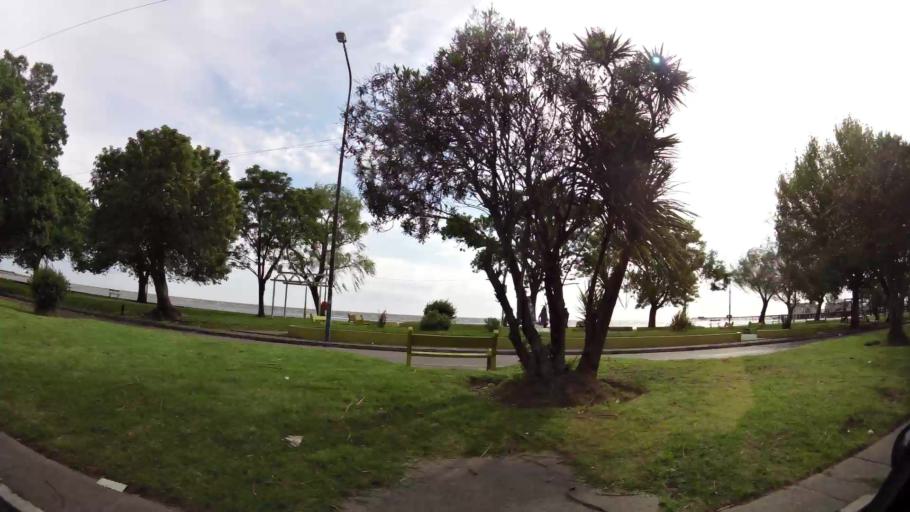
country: AR
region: Buenos Aires
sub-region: Partido de Quilmes
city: Quilmes
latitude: -34.7090
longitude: -58.2257
